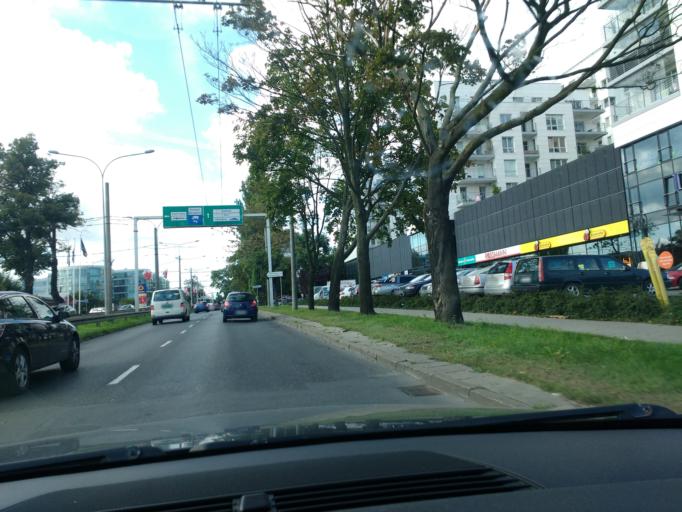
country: PL
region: Pomeranian Voivodeship
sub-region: Gdynia
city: Gdynia
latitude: 54.4905
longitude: 18.5420
